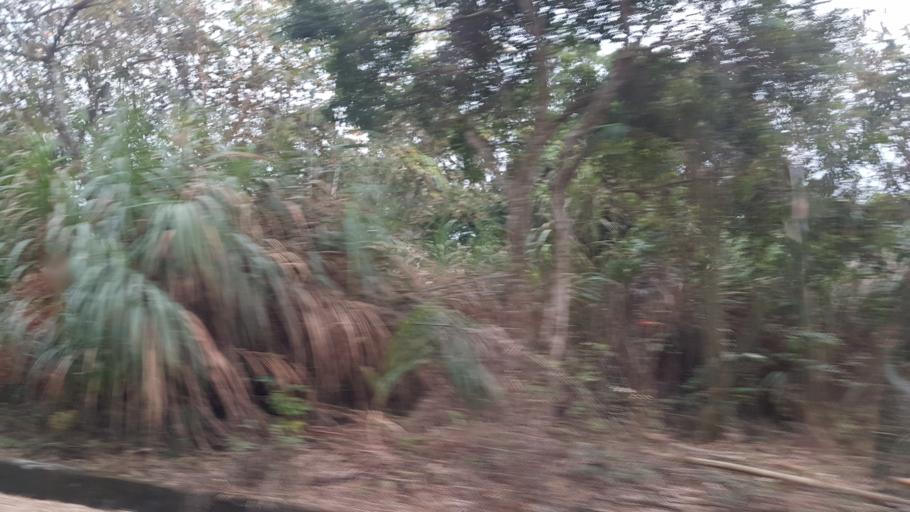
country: TW
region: Taiwan
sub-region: Chiayi
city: Jiayi Shi
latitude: 23.3222
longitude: 120.4810
